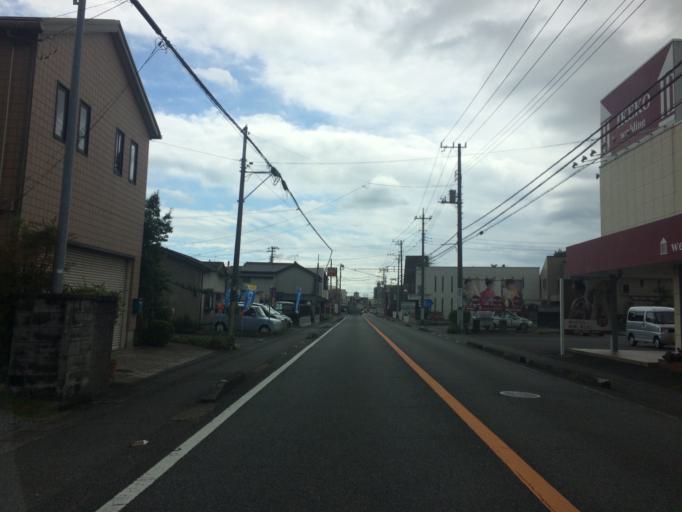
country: JP
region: Shizuoka
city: Fuji
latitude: 35.1638
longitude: 138.6496
